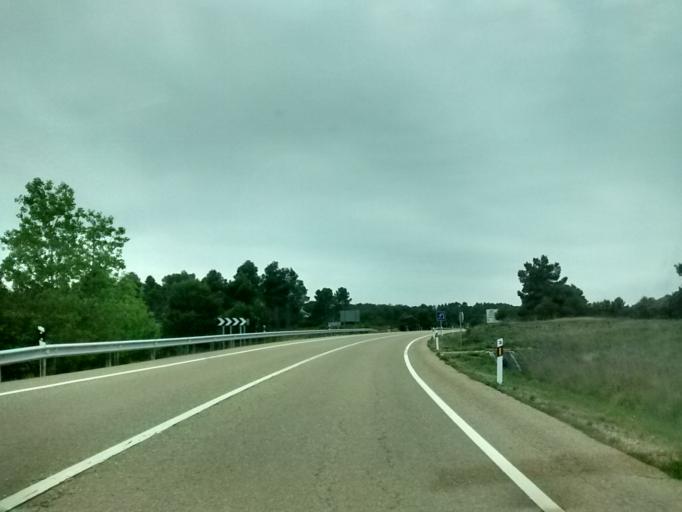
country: ES
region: Aragon
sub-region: Provincia de Teruel
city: Fornoles
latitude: 40.9189
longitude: -0.0187
